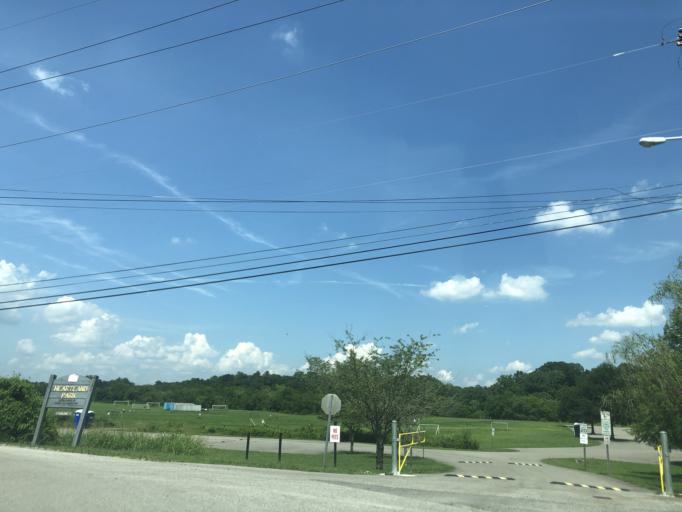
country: US
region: Tennessee
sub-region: Davidson County
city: Lakewood
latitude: 36.1855
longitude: -86.6679
